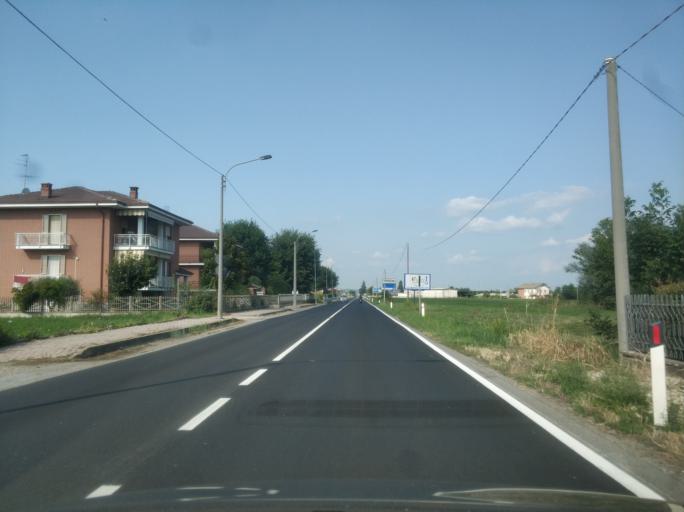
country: IT
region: Piedmont
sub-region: Provincia di Cuneo
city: Cervere
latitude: 44.6393
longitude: 7.7923
